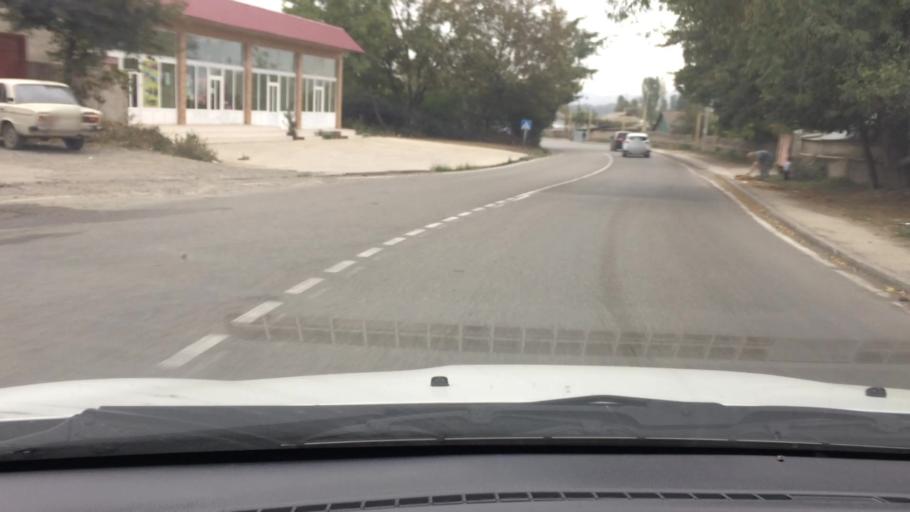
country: AM
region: Tavush
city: Bagratashen
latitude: 41.2475
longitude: 44.7990
